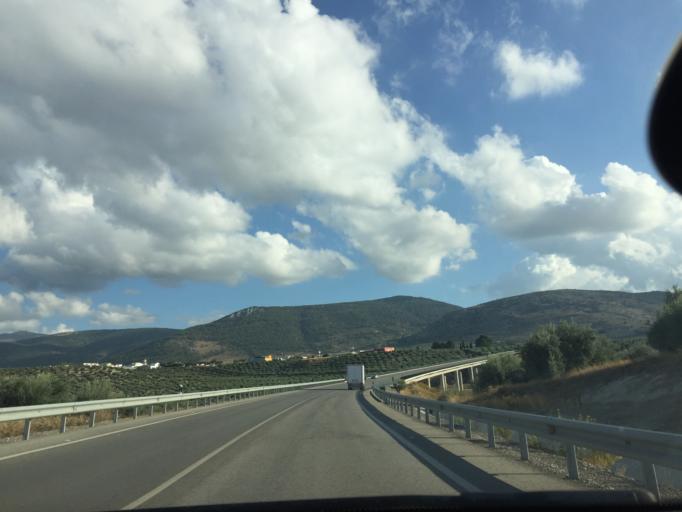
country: ES
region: Andalusia
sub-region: Provincia de Jaen
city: Mancha Real
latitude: 37.7967
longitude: -3.6232
